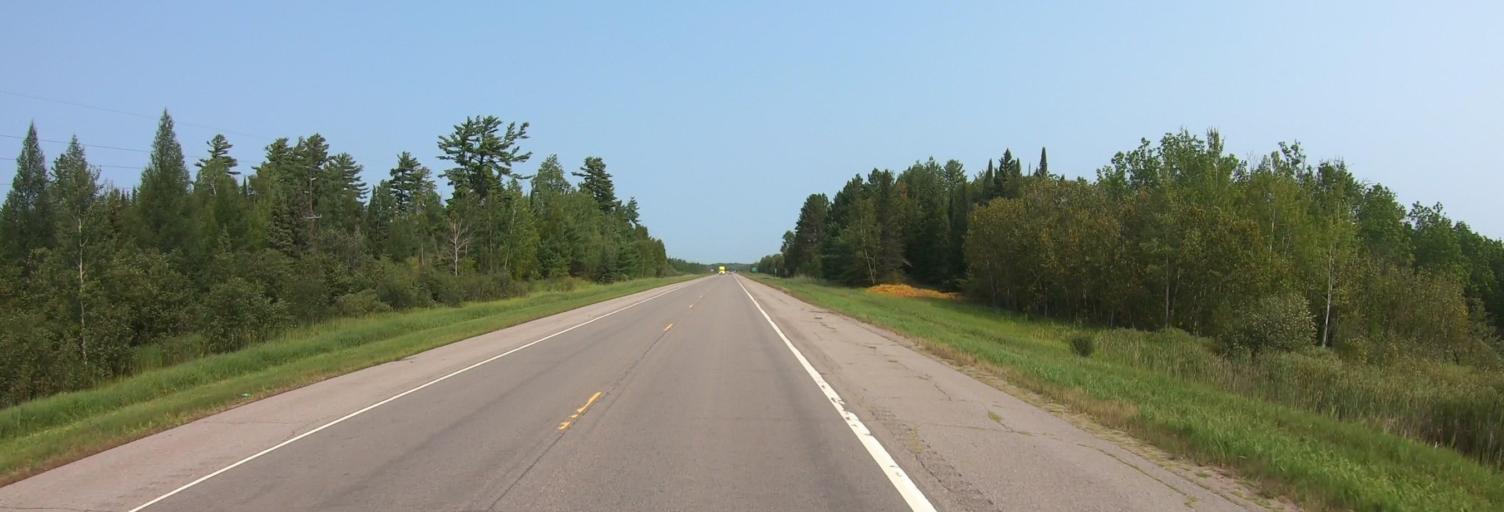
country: US
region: Minnesota
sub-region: Saint Louis County
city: Mountain Iron
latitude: 48.0107
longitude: -92.8305
